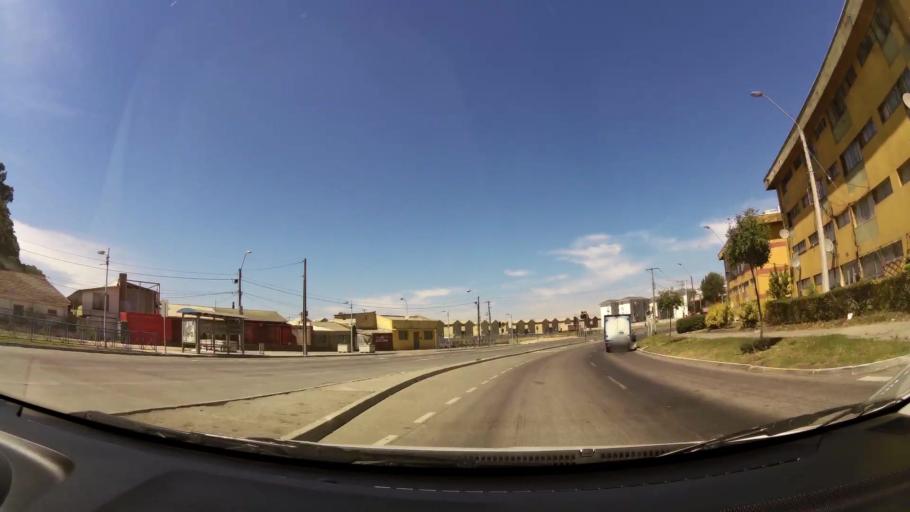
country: CL
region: Biobio
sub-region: Provincia de Concepcion
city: Talcahuano
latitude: -36.7244
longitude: -73.1067
